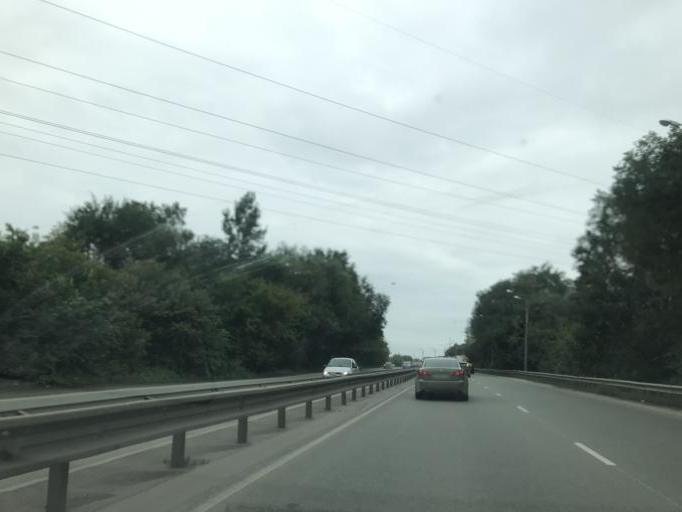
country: RU
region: Chelyabinsk
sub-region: Gorod Chelyabinsk
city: Chelyabinsk
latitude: 55.1711
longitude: 61.4274
